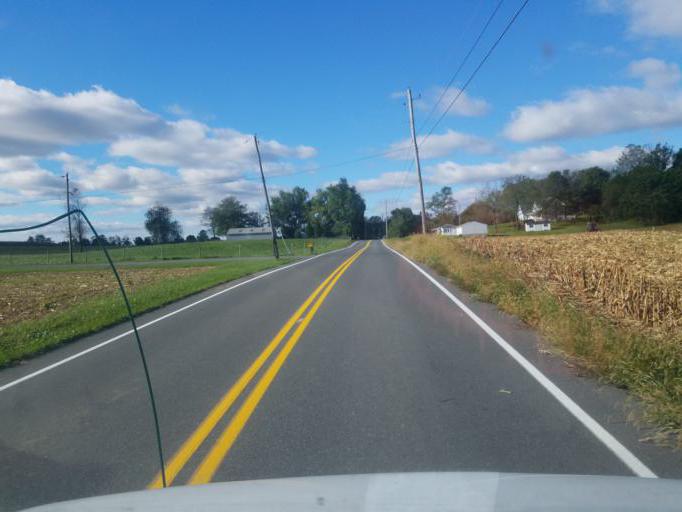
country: US
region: Pennsylvania
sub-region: Franklin County
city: Guilford Siding
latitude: 39.8420
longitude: -77.6206
